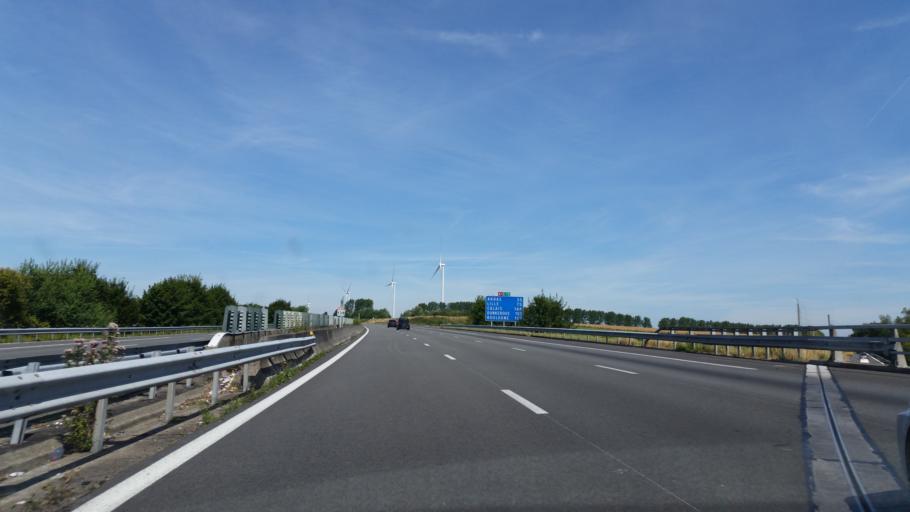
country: FR
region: Picardie
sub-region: Departement de la Somme
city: Moislains
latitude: 50.0221
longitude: 2.8838
